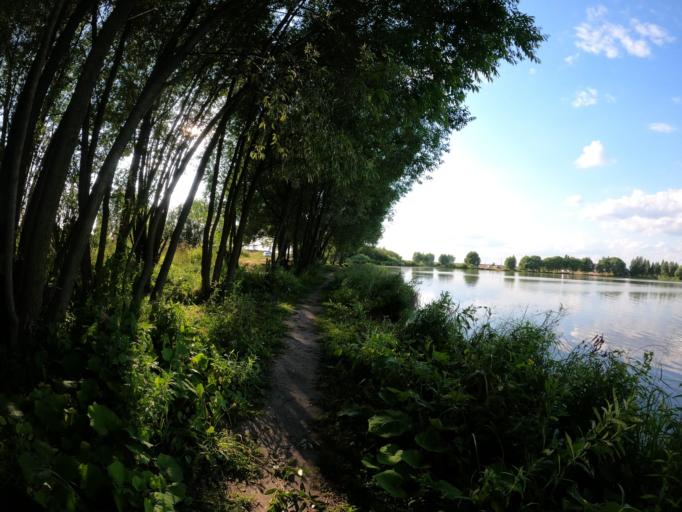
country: RU
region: Moskovskaya
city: Bronnitsy
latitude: 55.4710
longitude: 38.2550
